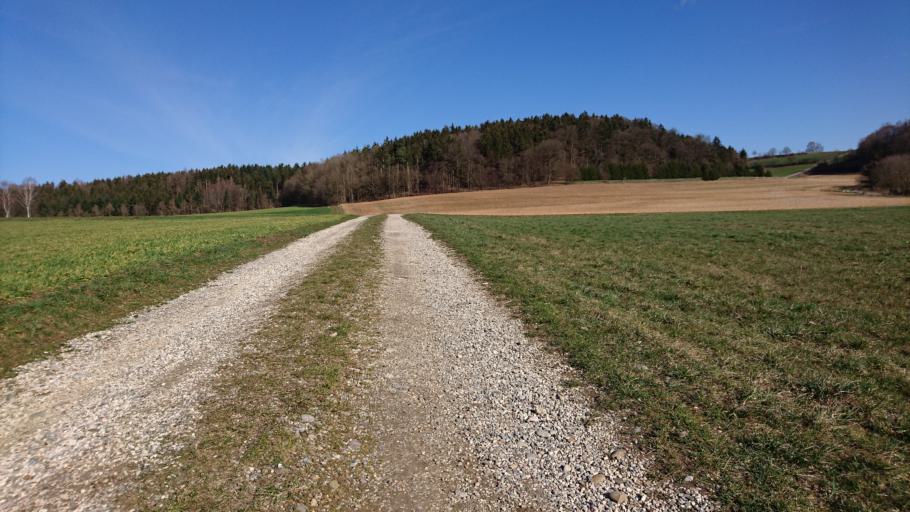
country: DE
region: Bavaria
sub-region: Swabia
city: Altenmunster
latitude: 48.4498
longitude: 10.6025
